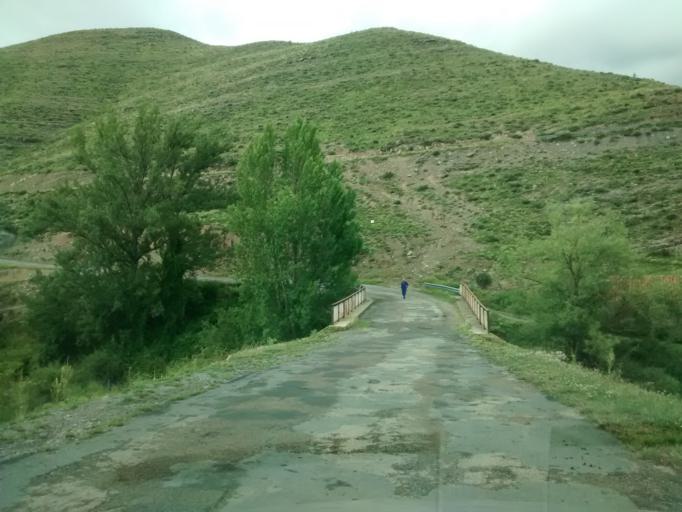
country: ES
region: La Rioja
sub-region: Provincia de La Rioja
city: San Roman de Cameros
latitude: 42.2184
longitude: -2.4667
